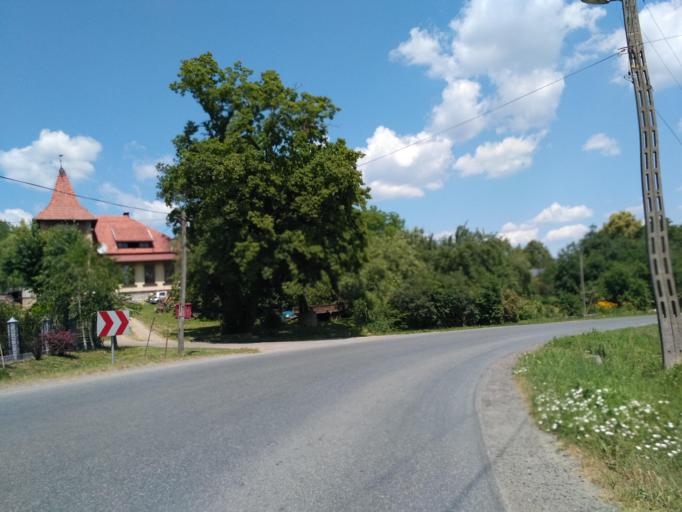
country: PL
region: Subcarpathian Voivodeship
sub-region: Powiat sanocki
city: Niebieszczany
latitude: 49.5558
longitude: 22.1441
